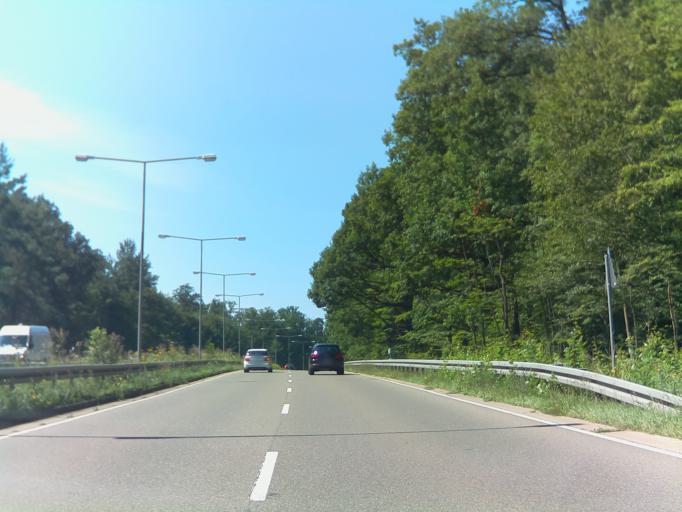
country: DE
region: Baden-Wuerttemberg
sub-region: Regierungsbezirk Stuttgart
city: Gerlingen
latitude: 48.7839
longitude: 9.0777
